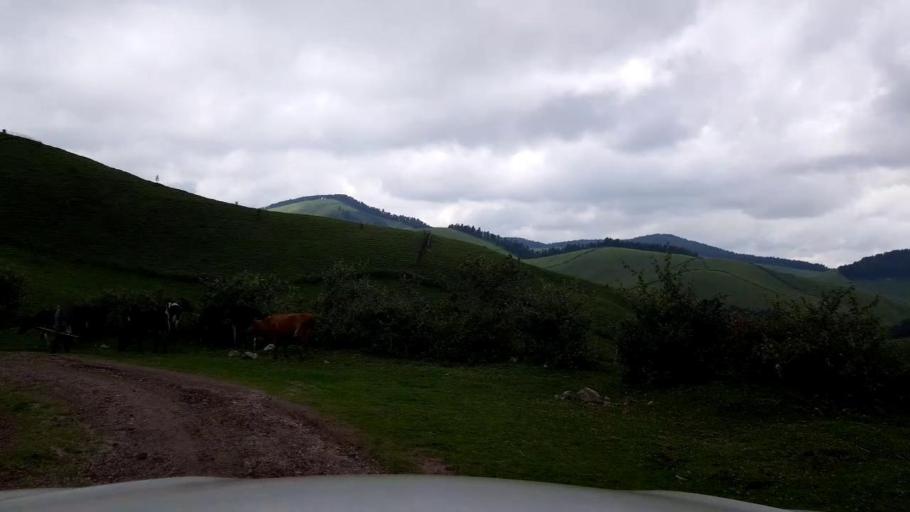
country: RW
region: Western Province
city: Gisenyi
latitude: -1.6786
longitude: 29.4176
